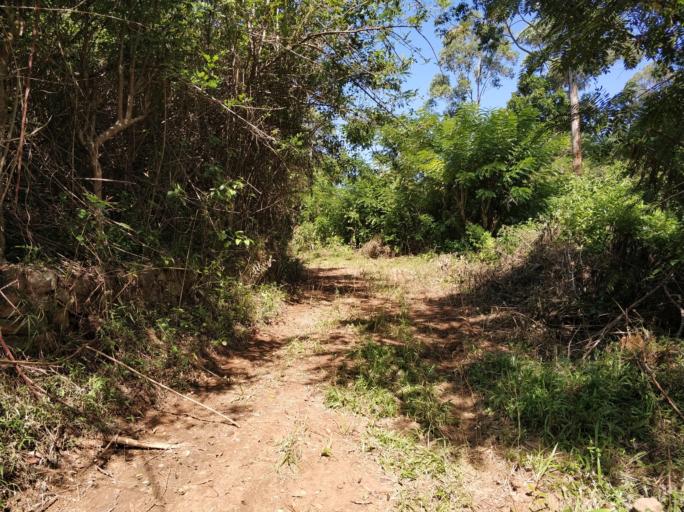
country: LK
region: Uva
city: Haputale
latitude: 6.8321
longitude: 81.0579
